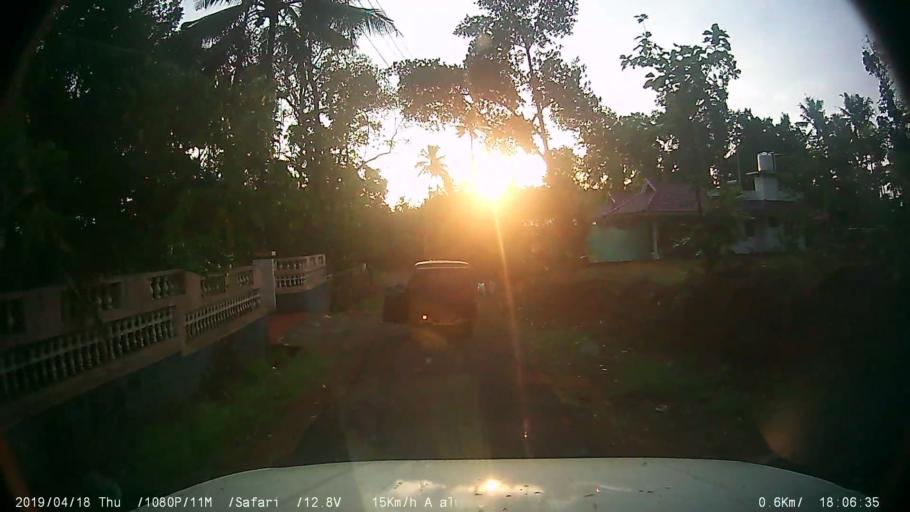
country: IN
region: Kerala
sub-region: Kottayam
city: Palackattumala
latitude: 9.7781
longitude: 76.5888
